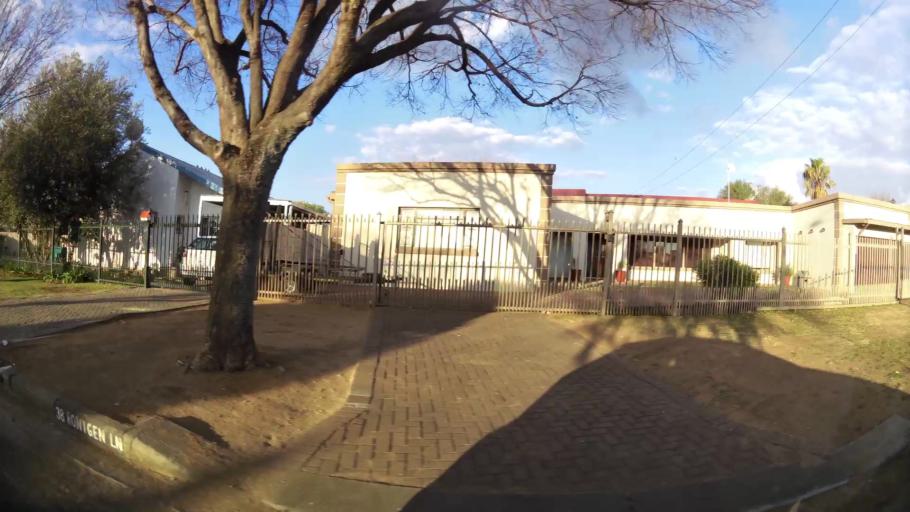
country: ZA
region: Orange Free State
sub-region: Mangaung Metropolitan Municipality
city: Bloemfontein
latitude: -29.1418
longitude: 26.1926
